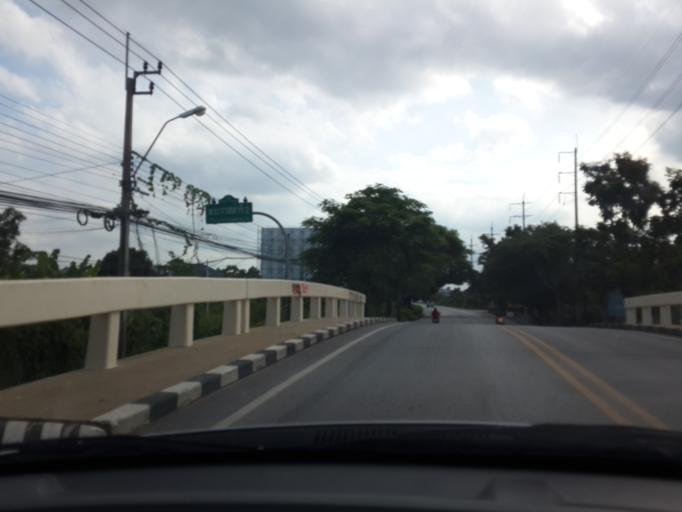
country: TH
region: Bangkok
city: Khlong Sam Wa
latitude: 13.8393
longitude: 100.7736
